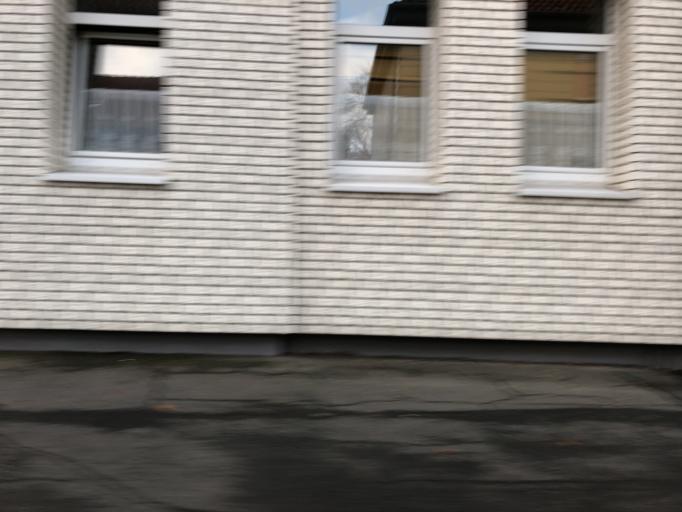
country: DE
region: Lower Saxony
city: Celle
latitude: 52.6241
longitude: 10.0879
